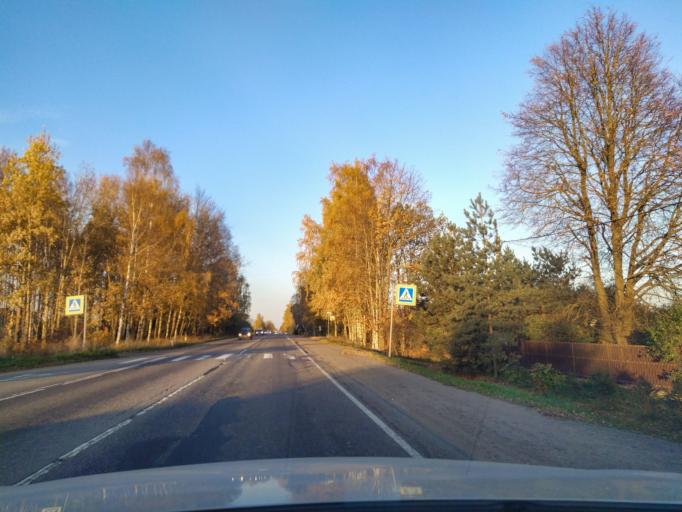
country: RU
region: Leningrad
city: Maloye Verevo
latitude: 59.6115
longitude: 30.1986
